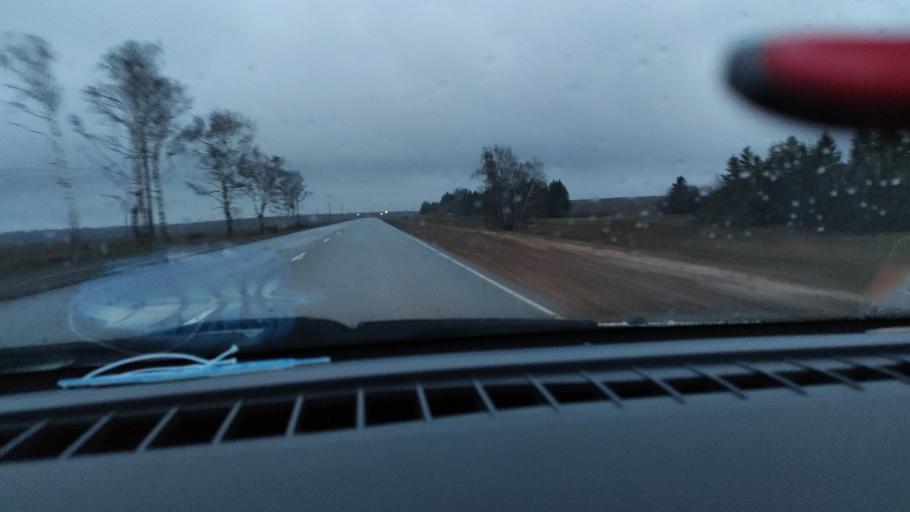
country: RU
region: Udmurtiya
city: Alnashi
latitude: 56.2991
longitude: 52.3472
